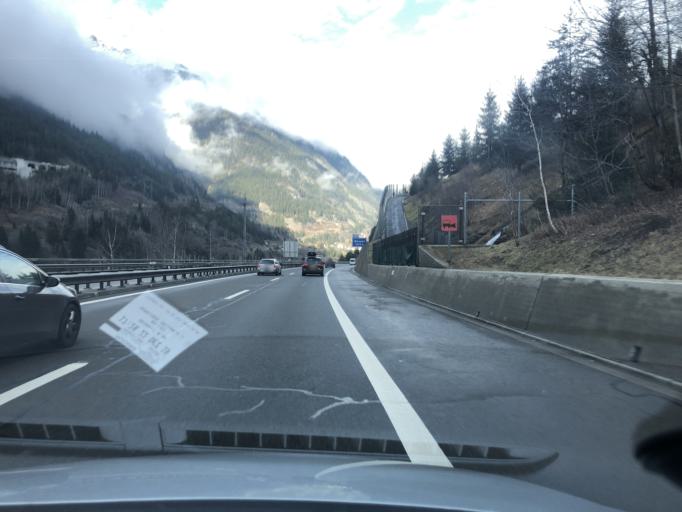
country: CH
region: Uri
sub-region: Uri
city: Andermatt
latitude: 46.6913
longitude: 8.5962
